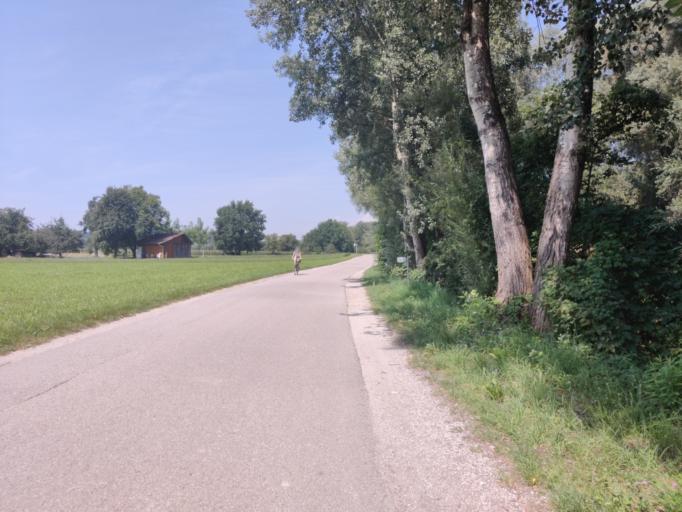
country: AT
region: Upper Austria
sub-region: Politischer Bezirk Urfahr-Umgebung
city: Ottensheim
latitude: 48.3290
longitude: 14.1661
